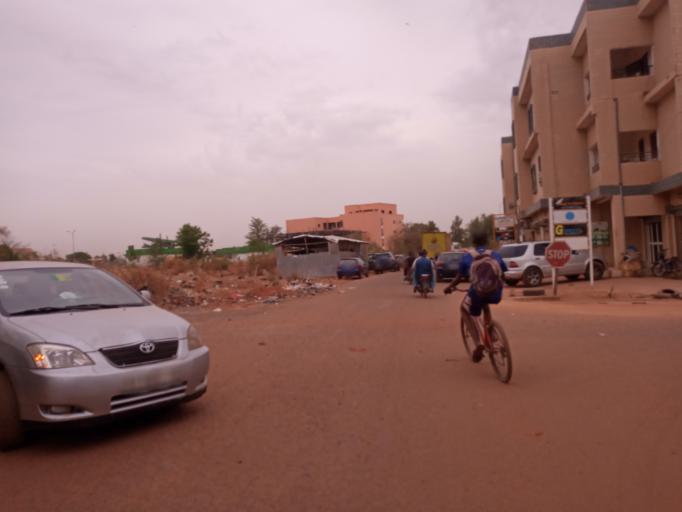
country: ML
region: Bamako
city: Bamako
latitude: 12.6375
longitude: -8.0204
